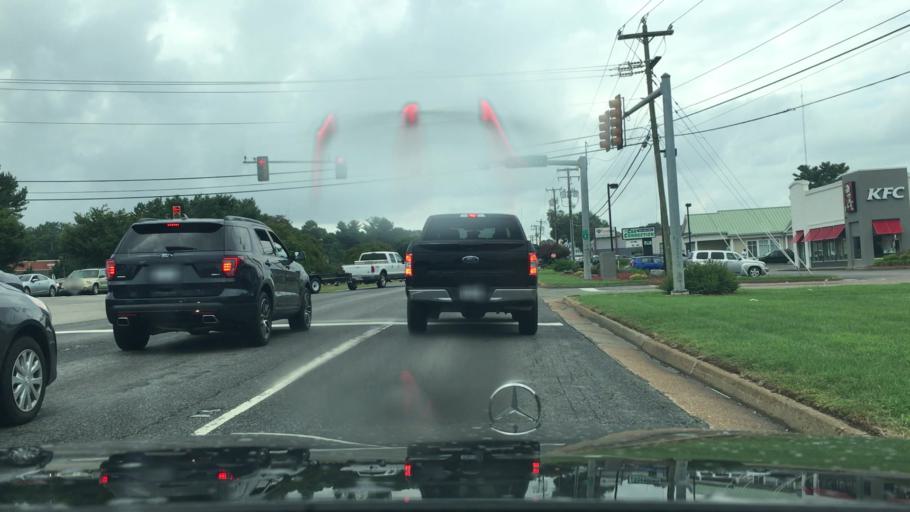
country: US
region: Virginia
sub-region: Chesterfield County
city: Bon Air
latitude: 37.4983
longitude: -77.5687
